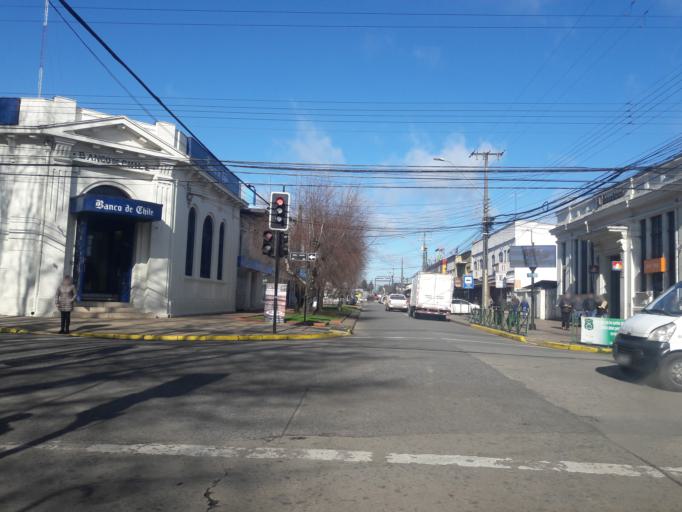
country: CL
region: Araucania
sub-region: Provincia de Malleco
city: Victoria
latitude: -38.2344
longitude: -72.3322
